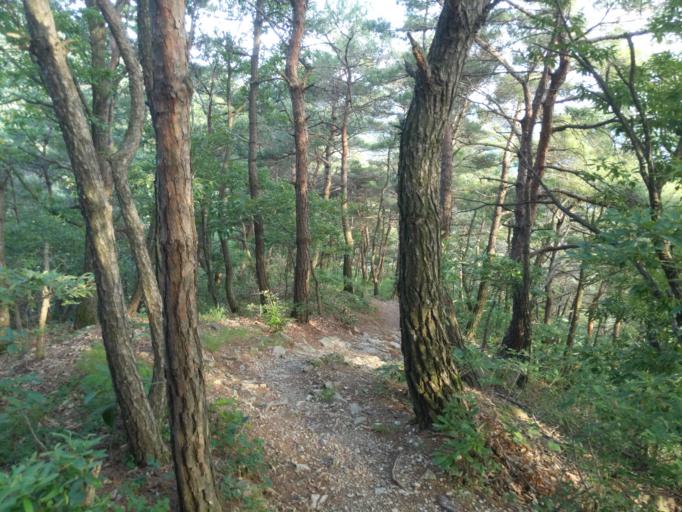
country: KR
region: Daegu
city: Hwawon
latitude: 35.7877
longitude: 128.5418
